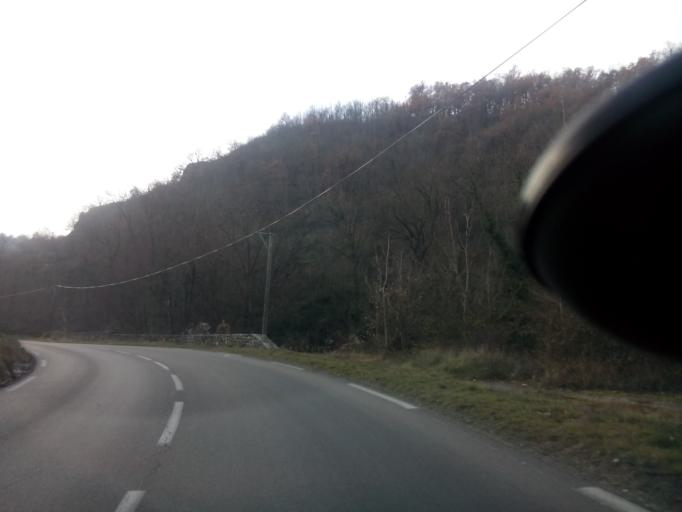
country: FR
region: Rhone-Alpes
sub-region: Departement de la Loire
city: Saint-Pierre-de-Boeuf
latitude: 45.3814
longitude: 4.7243
